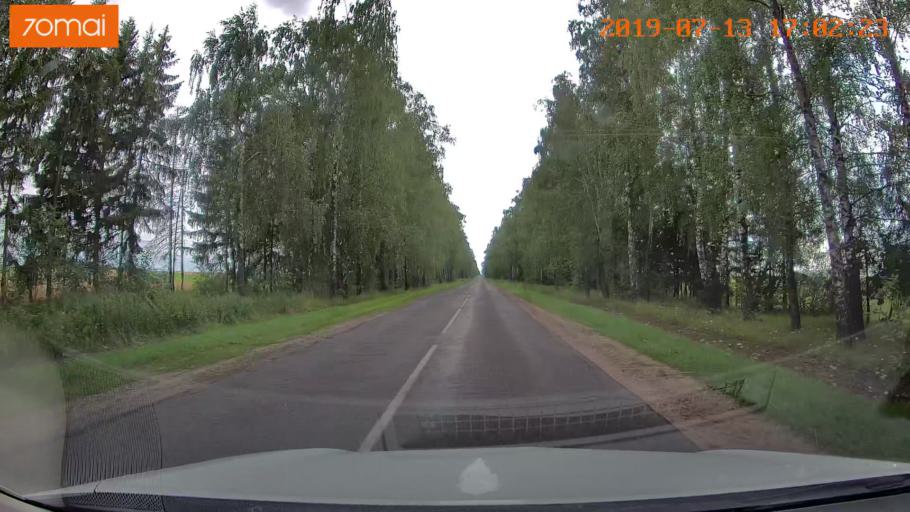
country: BY
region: Mogilev
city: Kirawsk
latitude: 53.2865
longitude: 29.3874
